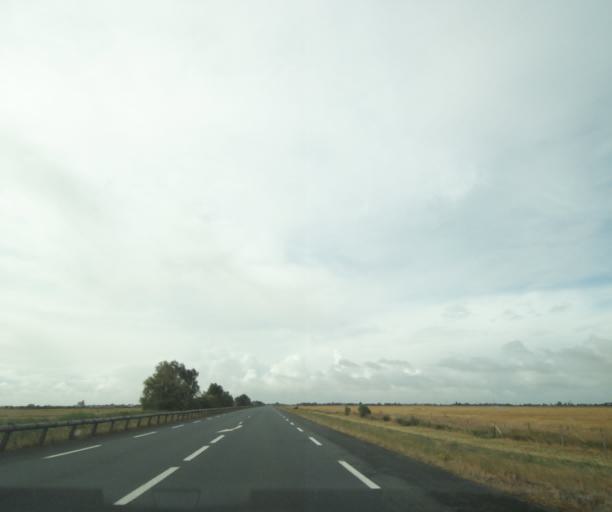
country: FR
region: Pays de la Loire
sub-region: Departement de la Vendee
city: Champagne-les-Marais
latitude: 46.3961
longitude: -1.0953
